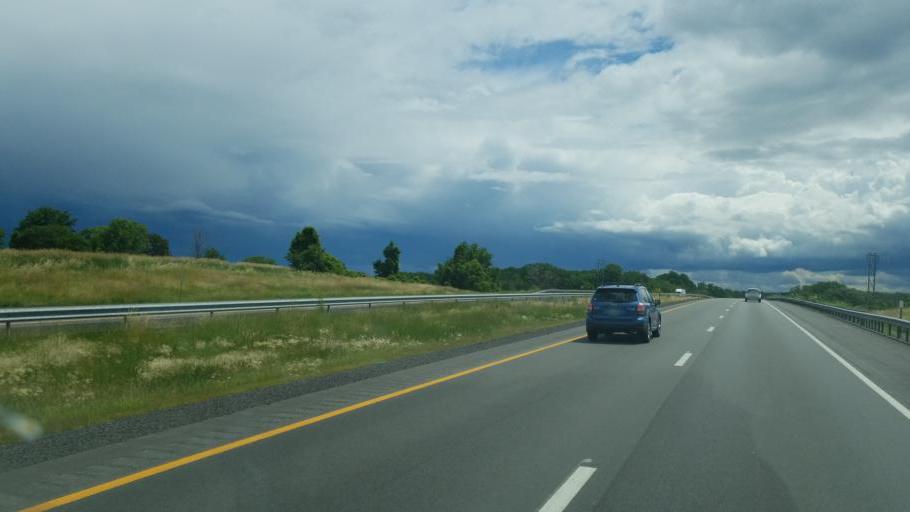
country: US
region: New York
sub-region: Monroe County
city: Scottsville
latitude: 43.0451
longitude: -77.7520
